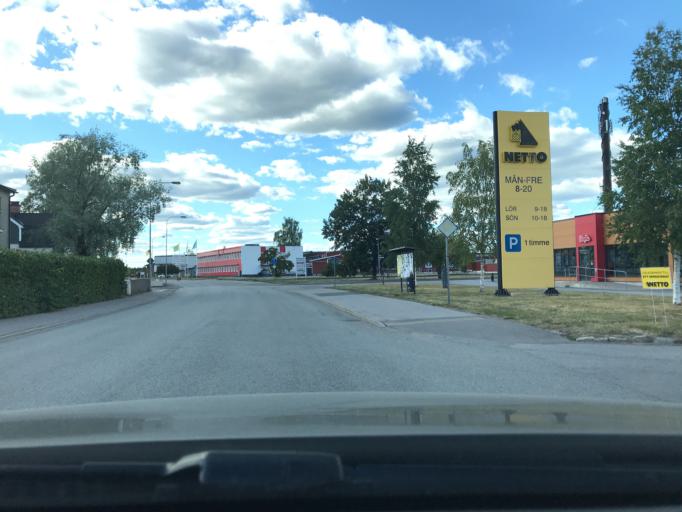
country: SE
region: Kalmar
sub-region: Hultsfreds Kommun
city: Hultsfred
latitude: 57.4932
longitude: 15.8399
